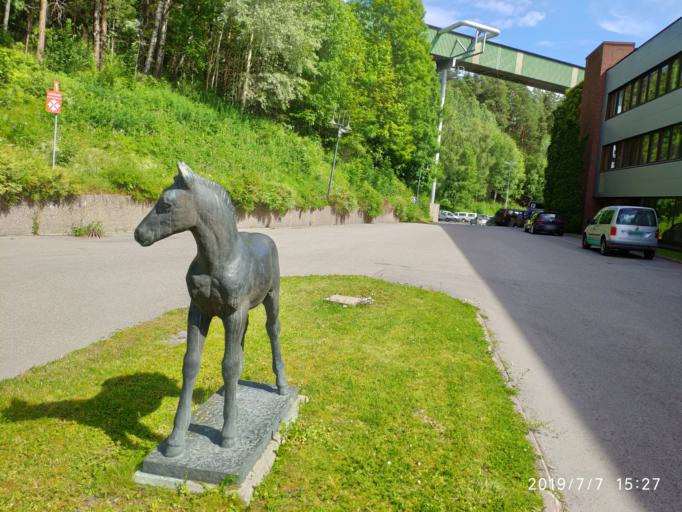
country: NO
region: Buskerud
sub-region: Ringerike
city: Honefoss
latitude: 60.1860
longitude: 10.2410
